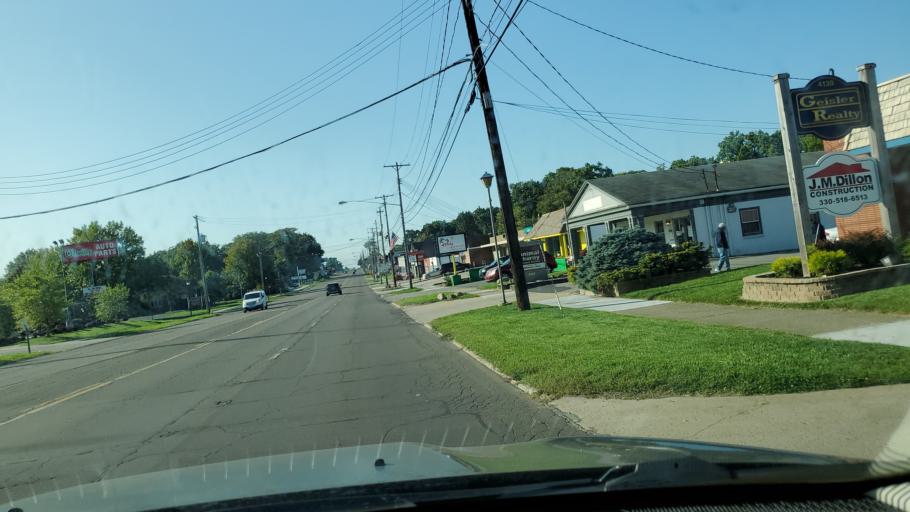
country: US
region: Ohio
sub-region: Mahoning County
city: Boardman
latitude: 41.0578
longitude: -80.6629
